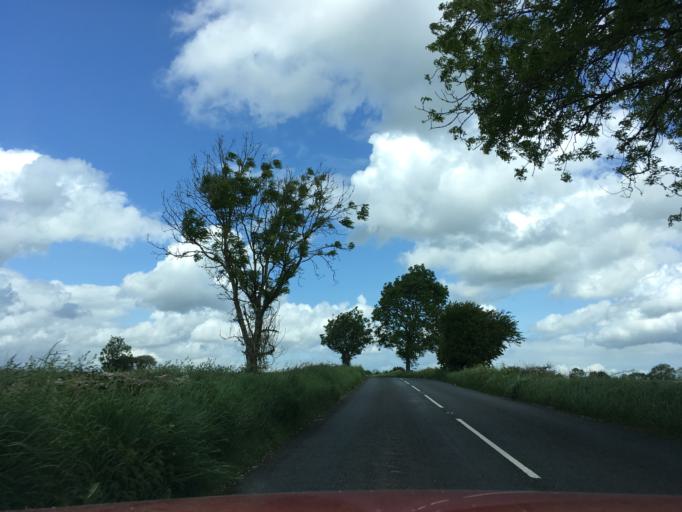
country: GB
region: England
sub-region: Gloucestershire
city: Shurdington
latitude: 51.7949
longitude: -2.1275
